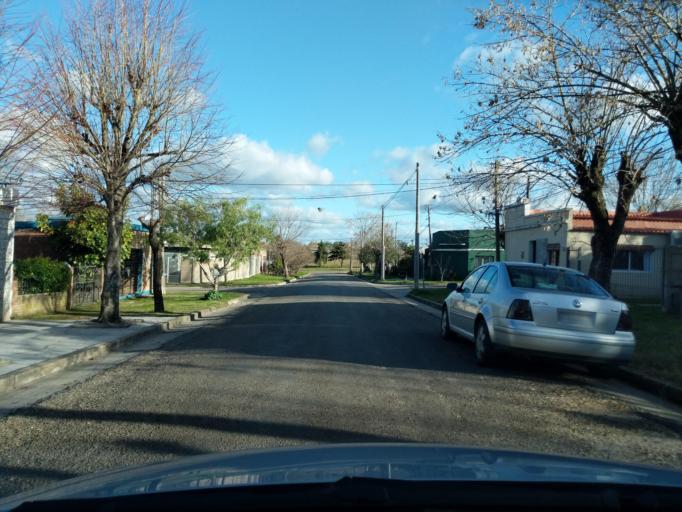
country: UY
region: Florida
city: Florida
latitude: -34.0996
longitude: -56.2302
